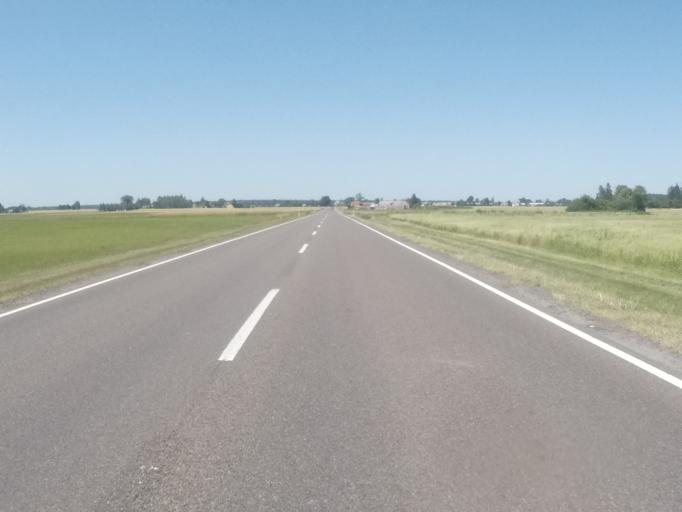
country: PL
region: Lublin Voivodeship
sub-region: Powiat bialski
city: Miedzyrzec Podlaski
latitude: 52.0669
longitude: 22.7330
